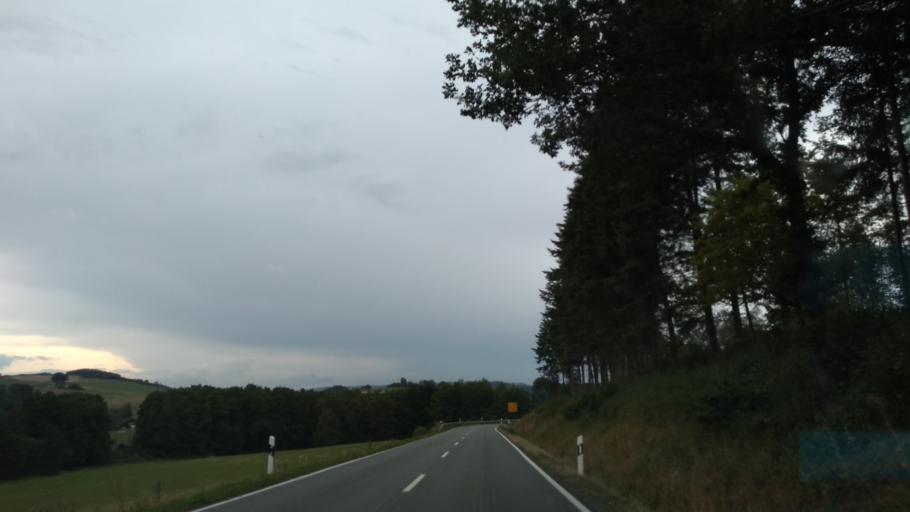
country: DE
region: North Rhine-Westphalia
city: Balve
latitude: 51.3047
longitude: 7.9076
